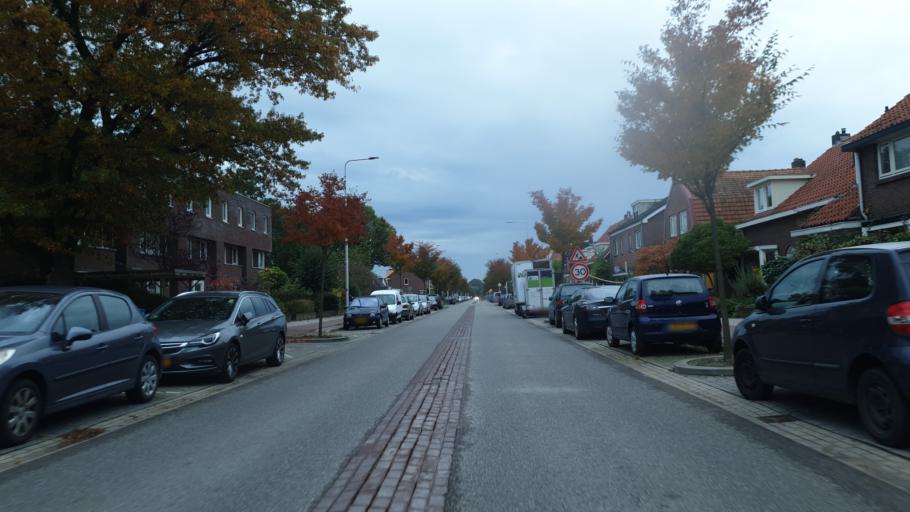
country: NL
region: Gelderland
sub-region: Gemeente Nijmegen
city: Nijmegen
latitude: 51.8153
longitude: 5.8483
